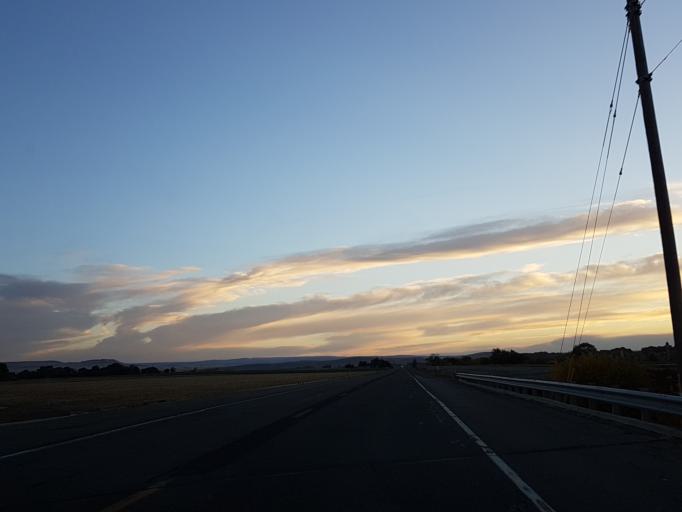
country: US
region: Oregon
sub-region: Malheur County
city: Vale
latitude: 43.9672
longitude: -117.2723
